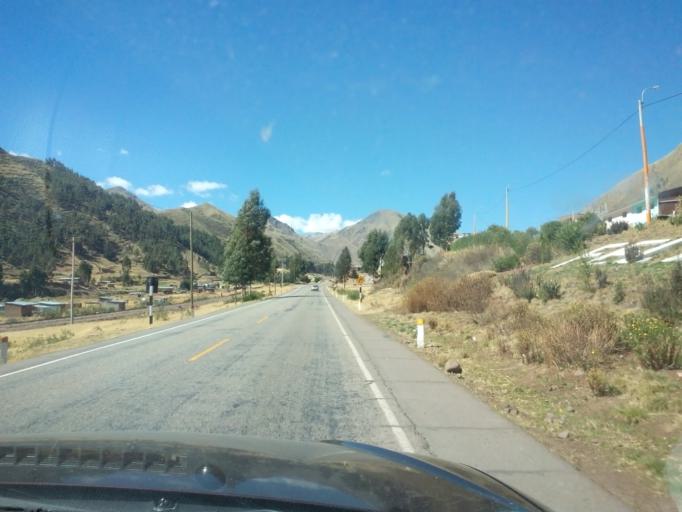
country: PE
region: Cusco
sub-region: Provincia de Canchis
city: Marangani
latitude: -14.3521
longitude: -71.1727
